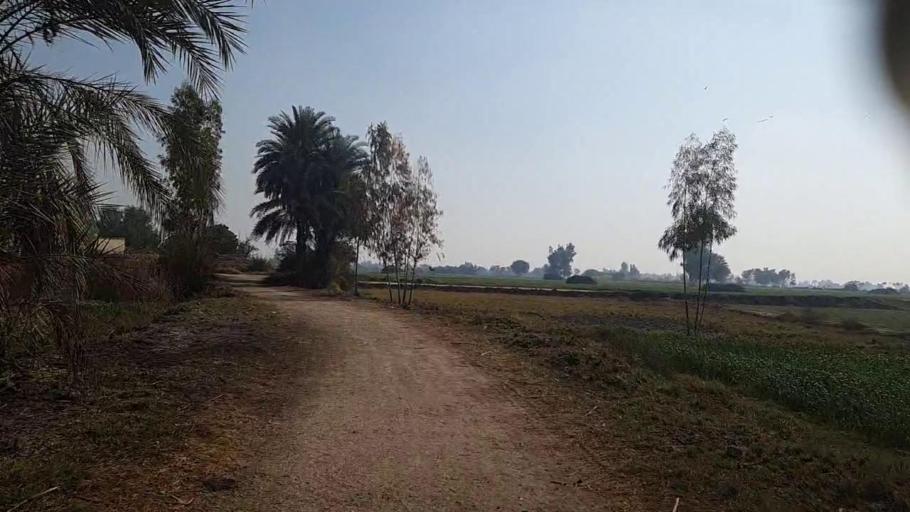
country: PK
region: Sindh
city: Khairpur
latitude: 27.9259
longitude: 69.6681
